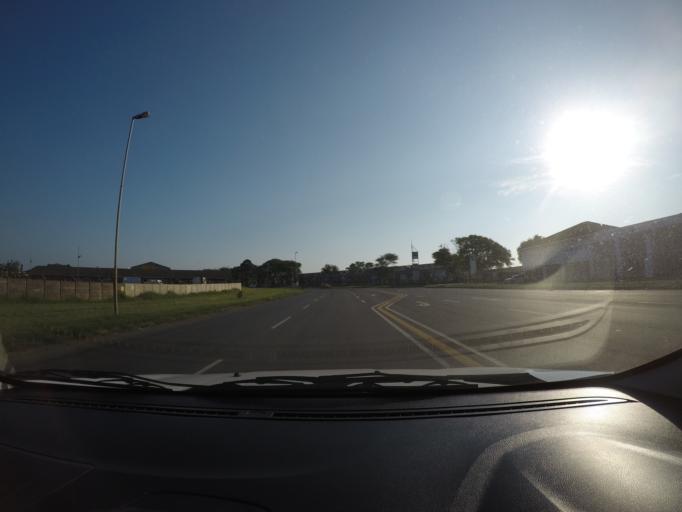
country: ZA
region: KwaZulu-Natal
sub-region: uThungulu District Municipality
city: Richards Bay
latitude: -28.7541
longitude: 32.0258
